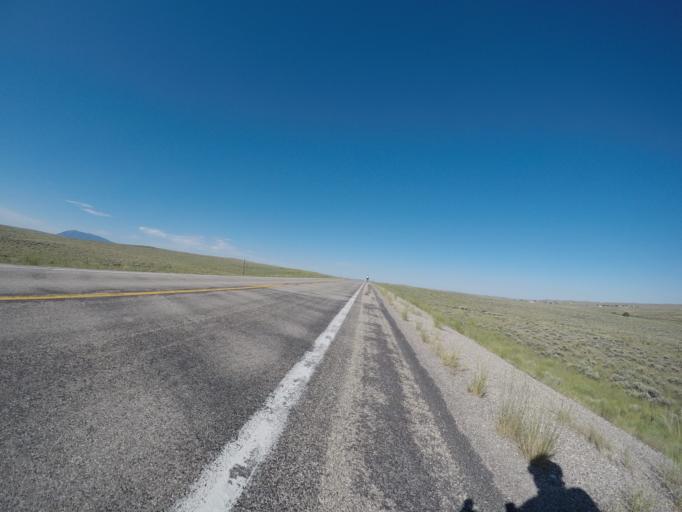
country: US
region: Wyoming
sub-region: Carbon County
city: Saratoga
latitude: 41.8719
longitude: -106.5005
